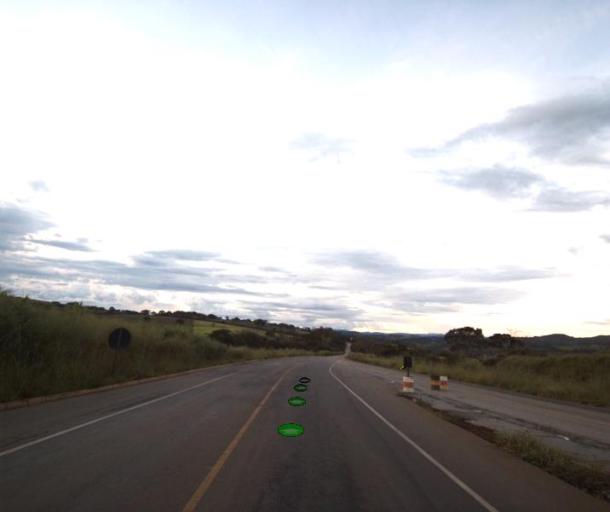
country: BR
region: Goias
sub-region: Anapolis
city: Anapolis
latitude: -16.1787
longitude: -49.0428
